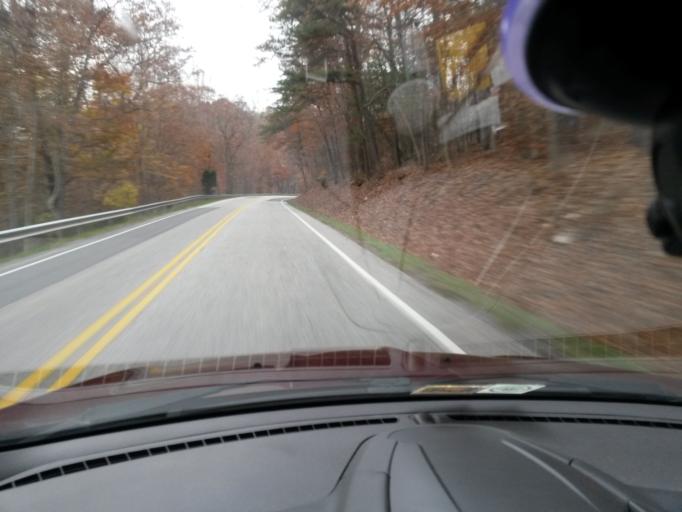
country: US
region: Virginia
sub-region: Rockbridge County
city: Glasgow
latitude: 37.6794
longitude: -79.4066
